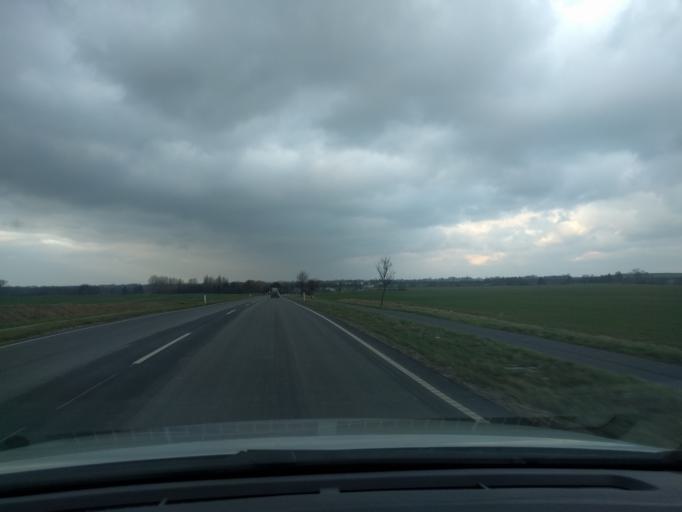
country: DK
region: South Denmark
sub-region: Nyborg Kommune
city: Nyborg
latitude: 55.3257
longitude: 10.7650
